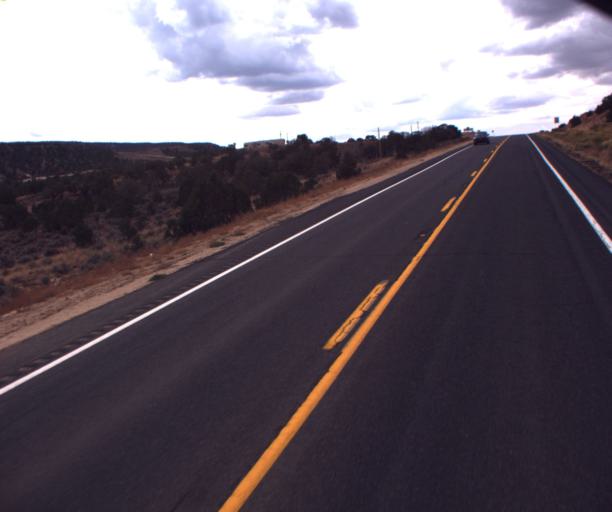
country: US
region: Arizona
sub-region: Navajo County
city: Kayenta
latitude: 36.5634
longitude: -110.4973
